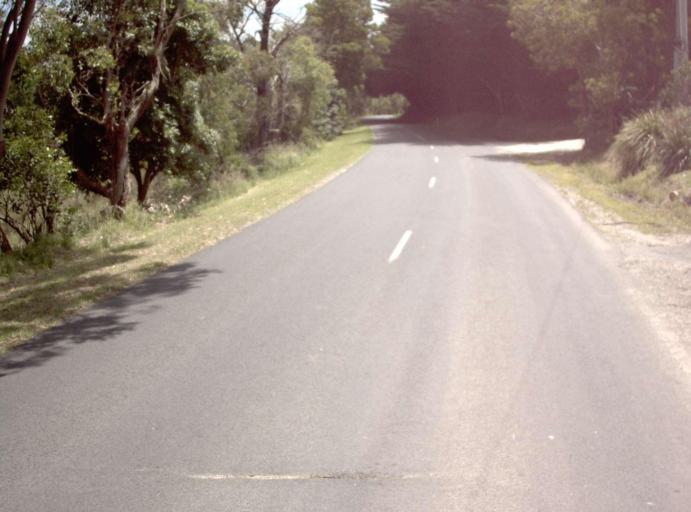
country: AU
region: Victoria
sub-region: Bass Coast
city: North Wonthaggi
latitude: -38.6984
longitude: 146.0878
